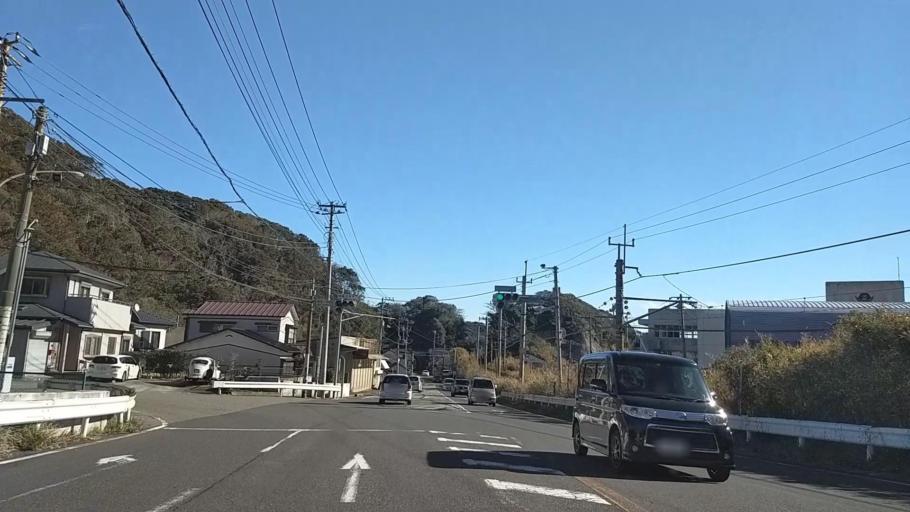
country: JP
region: Chiba
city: Katsuura
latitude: 35.1408
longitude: 140.2704
